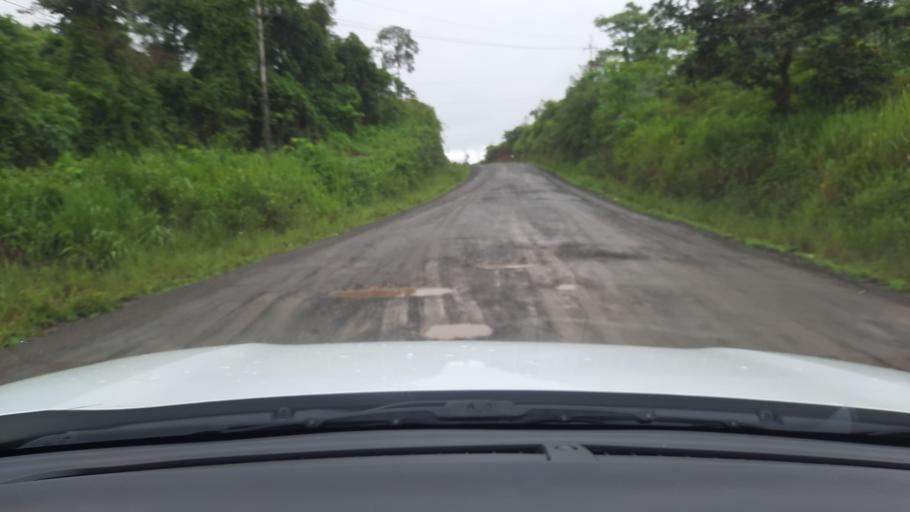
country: CR
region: Alajuela
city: San Jose
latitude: 11.0144
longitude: -85.3341
